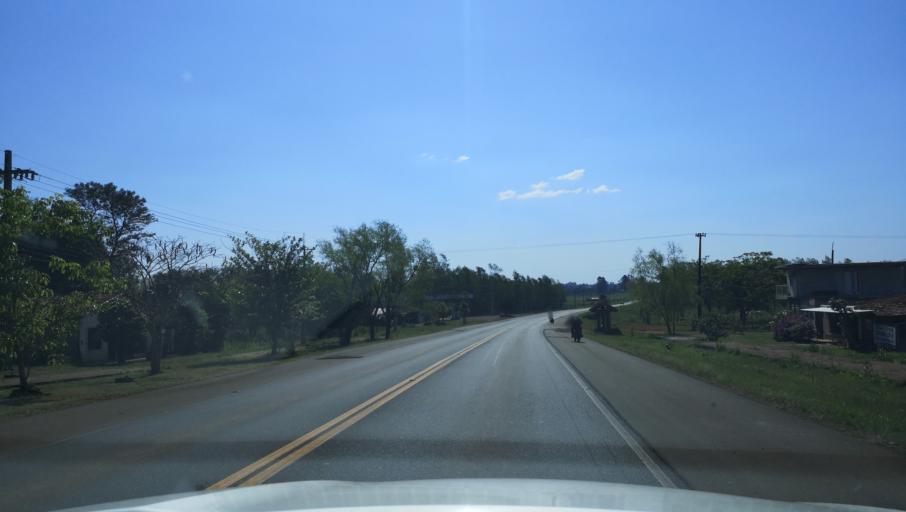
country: PY
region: Misiones
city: Santiago
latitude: -27.0430
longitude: -56.6572
